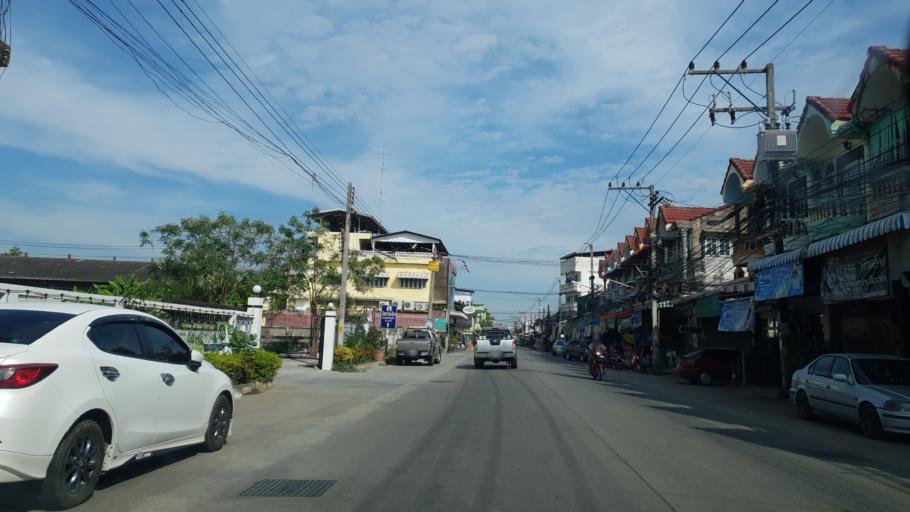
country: TH
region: Phitsanulok
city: Phitsanulok
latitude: 16.8083
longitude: 100.2676
